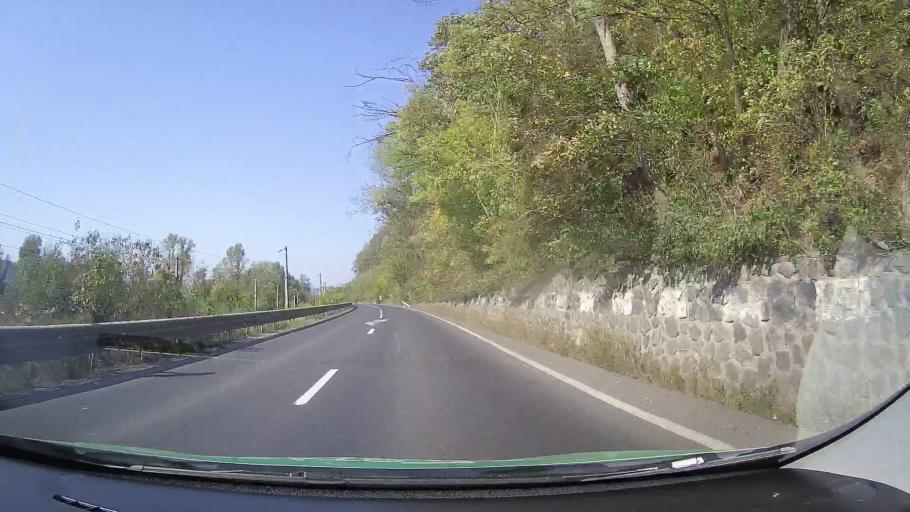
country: RO
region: Arad
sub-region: Comuna Savarsin
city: Savarsin
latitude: 46.0011
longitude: 22.2842
